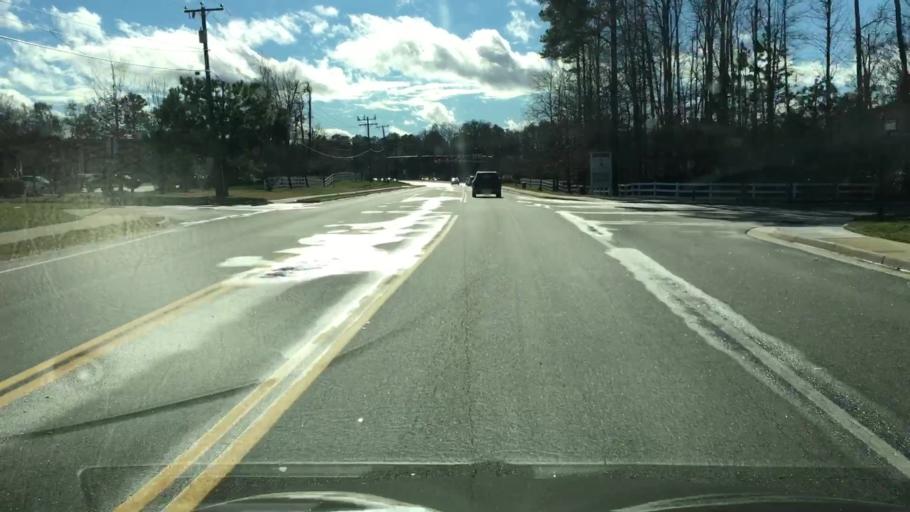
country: US
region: Virginia
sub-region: Chesterfield County
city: Bon Air
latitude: 37.5219
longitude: -77.6044
